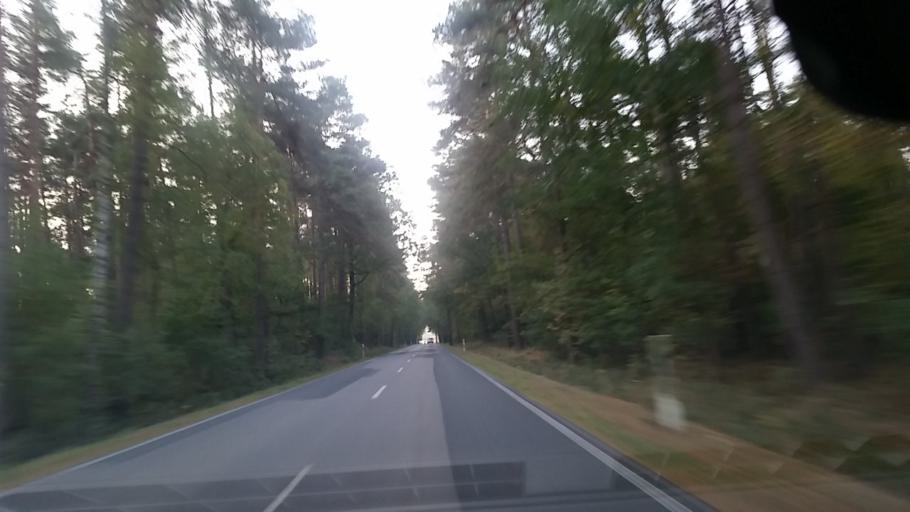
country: DE
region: Lower Saxony
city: Tulau
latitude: 52.6320
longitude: 10.8117
